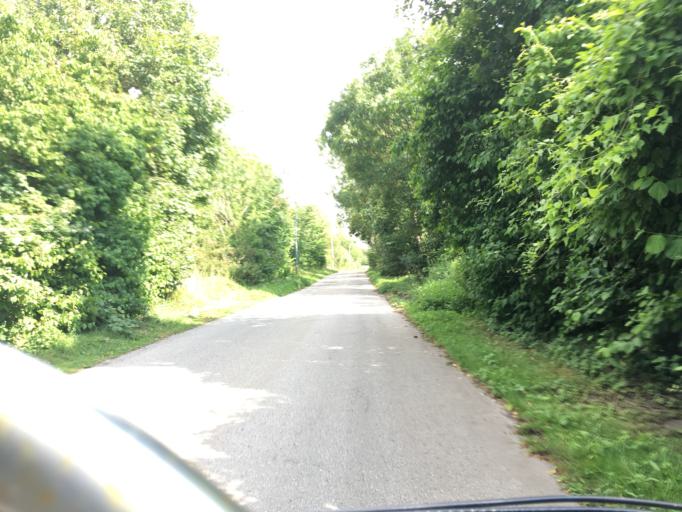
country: SE
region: Skane
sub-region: Lunds Kommun
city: Lund
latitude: 55.6948
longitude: 13.1648
